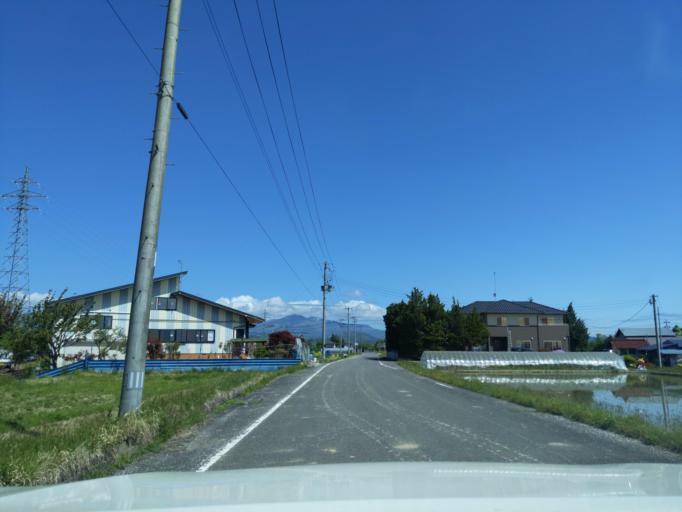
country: JP
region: Fukushima
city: Koriyama
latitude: 37.4401
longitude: 140.3277
